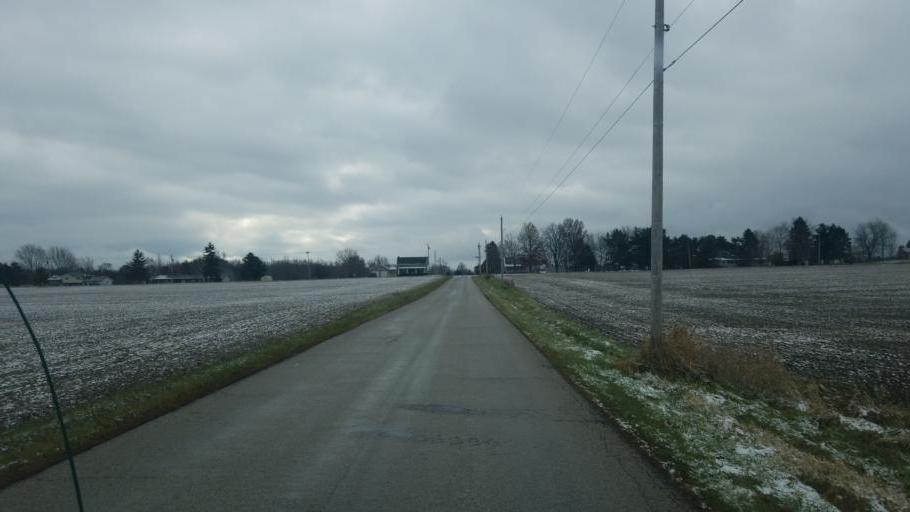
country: US
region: Ohio
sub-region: Richland County
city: Ontario
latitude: 40.8601
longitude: -82.5520
